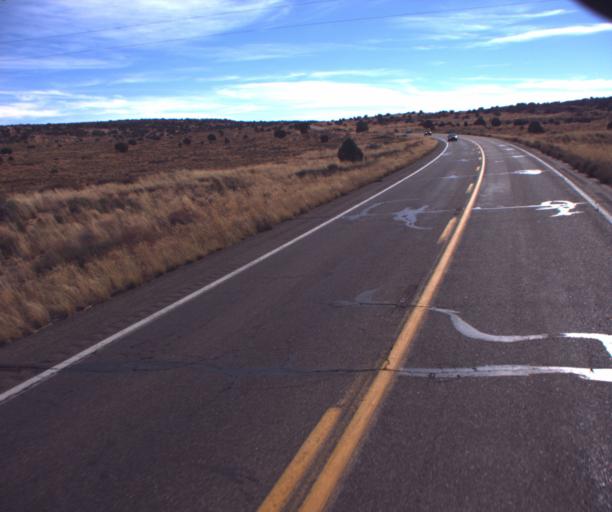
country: US
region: Arizona
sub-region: Coconino County
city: Kaibito
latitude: 36.5823
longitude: -111.1458
